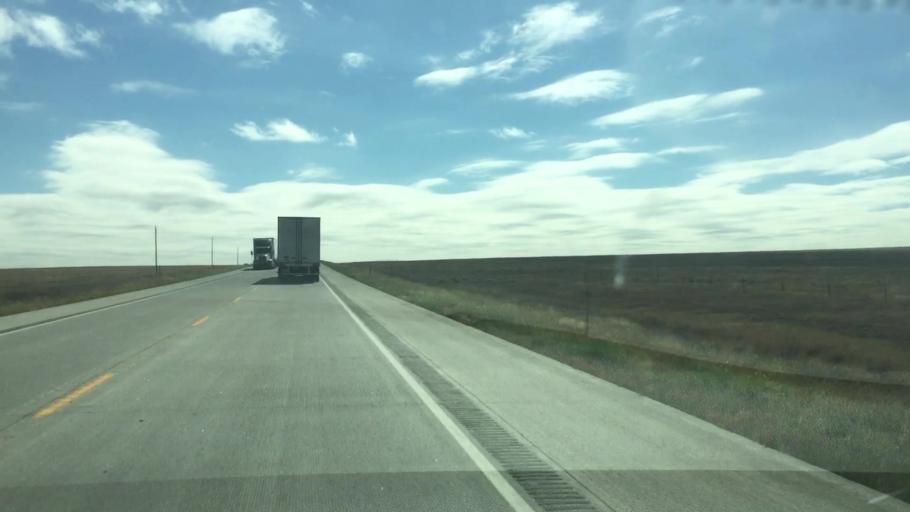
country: US
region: Colorado
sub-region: Lincoln County
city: Hugo
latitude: 39.0268
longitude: -103.3193
